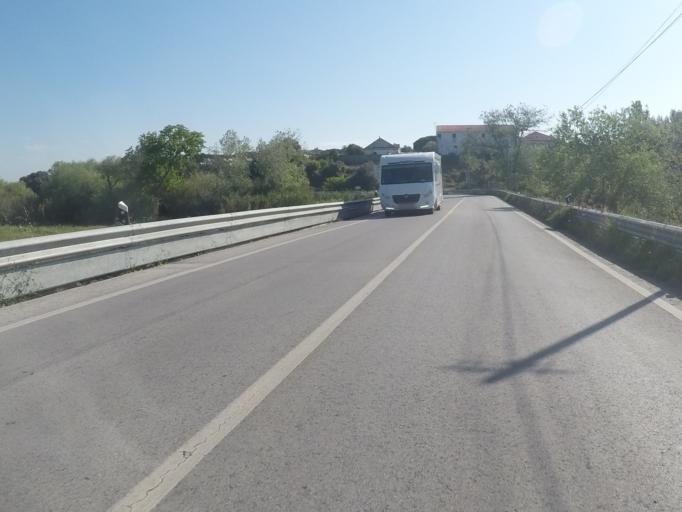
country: PT
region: Setubal
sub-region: Sesimbra
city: Sesimbra
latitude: 38.5017
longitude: -9.1497
